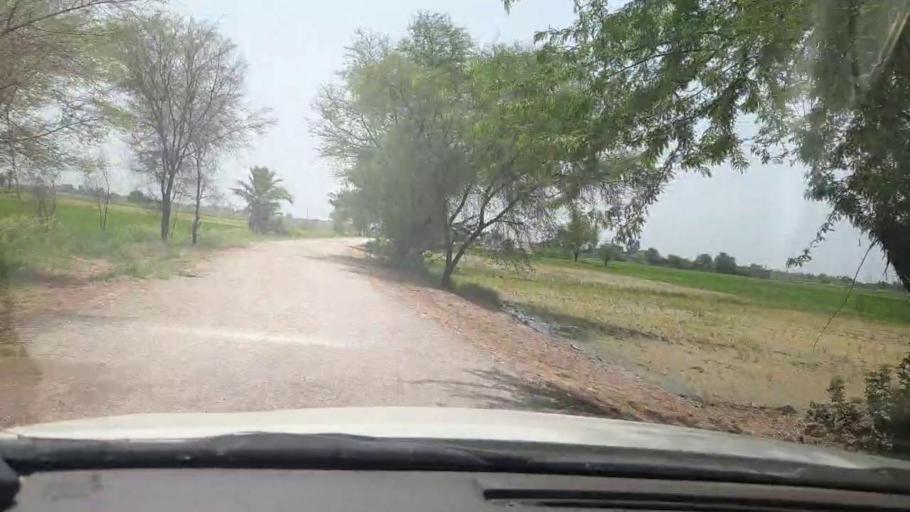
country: PK
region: Sindh
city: Garhi Yasin
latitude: 27.9110
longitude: 68.5541
